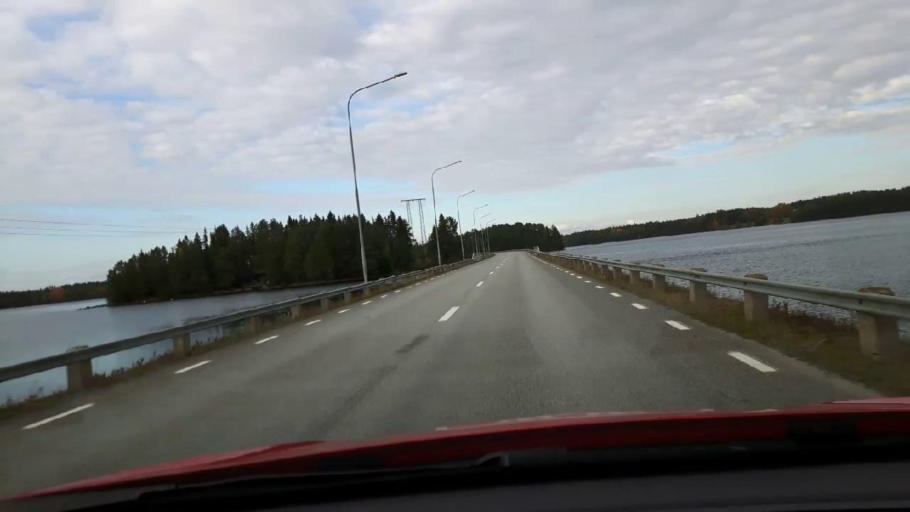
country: SE
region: Jaemtland
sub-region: Krokoms Kommun
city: Valla
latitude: 63.2464
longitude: 13.9995
